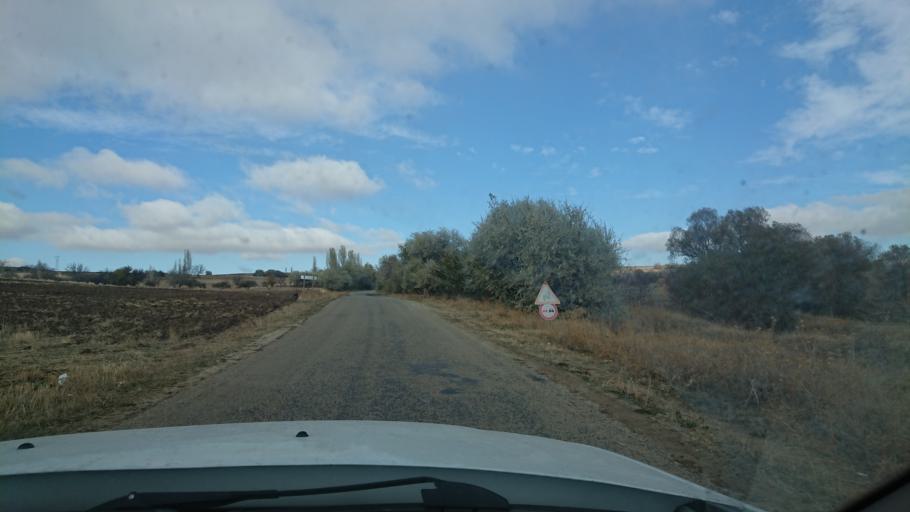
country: TR
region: Aksaray
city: Agacoren
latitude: 38.8290
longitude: 33.9569
